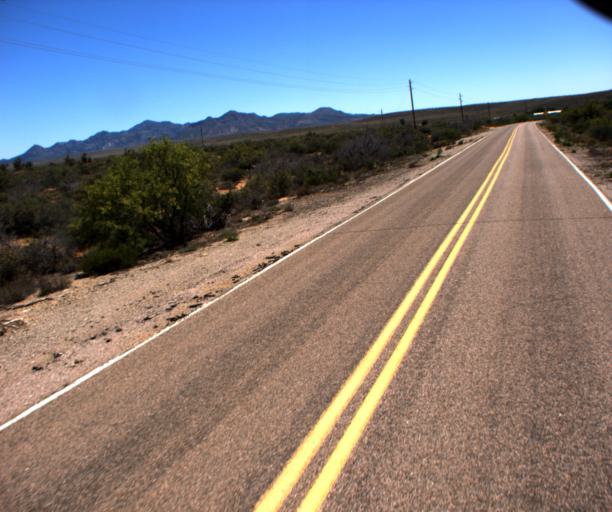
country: US
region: Arizona
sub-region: Yavapai County
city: Congress
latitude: 34.4276
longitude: -112.9164
